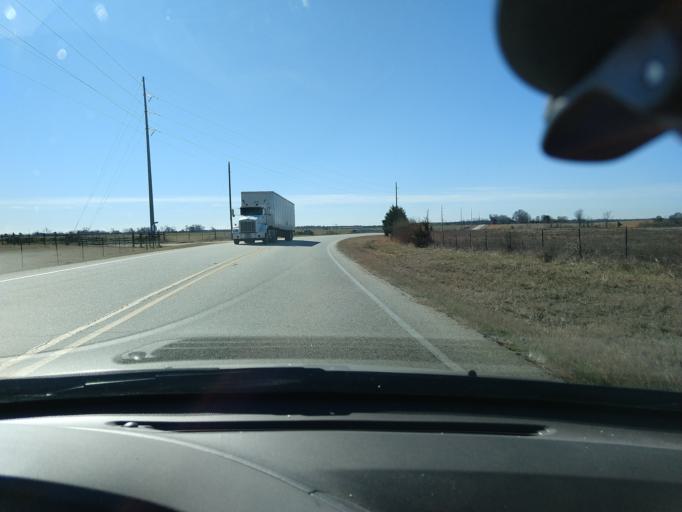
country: US
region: Georgia
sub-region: Newton County
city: Covington
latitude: 33.4987
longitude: -83.7358
